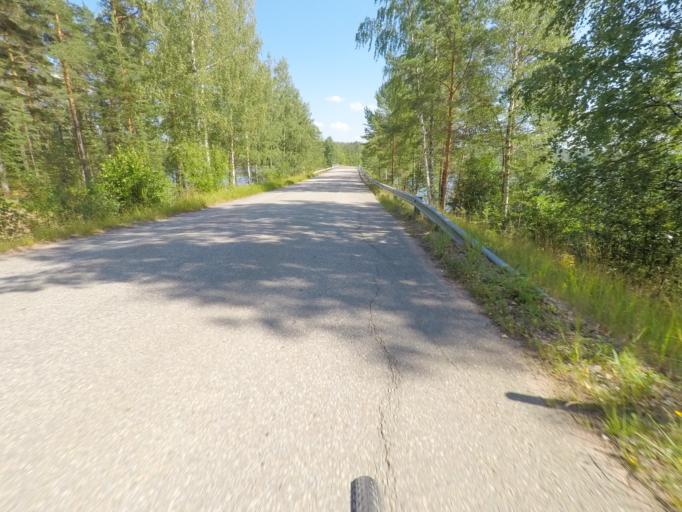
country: FI
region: Southern Savonia
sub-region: Mikkeli
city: Puumala
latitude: 61.4211
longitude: 28.1097
